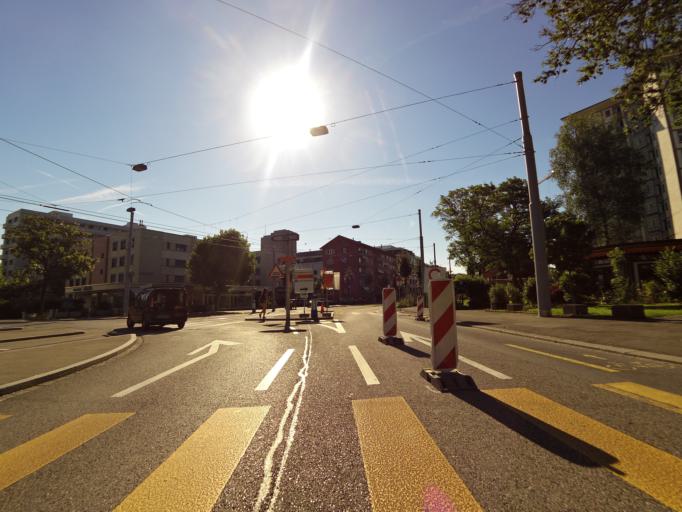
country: CH
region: Zurich
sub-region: Bezirk Zuerich
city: Zuerich (Kreis 4) / Hard
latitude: 47.3810
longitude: 8.5037
